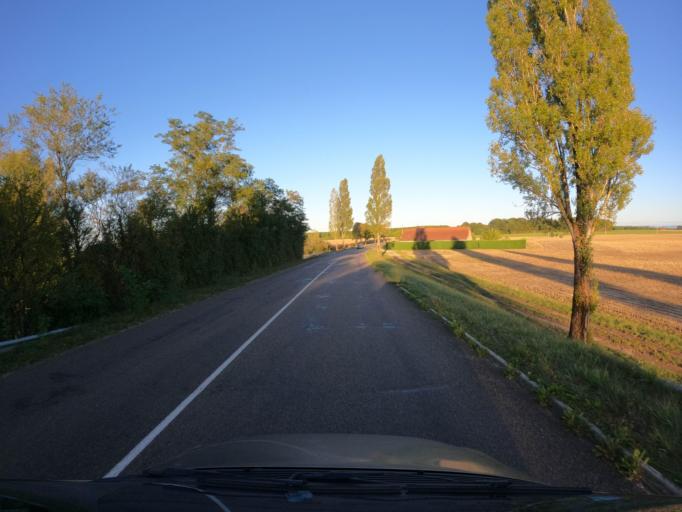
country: FR
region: Bourgogne
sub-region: Departement de Saone-et-Loire
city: Mervans
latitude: 46.7486
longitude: 5.1922
